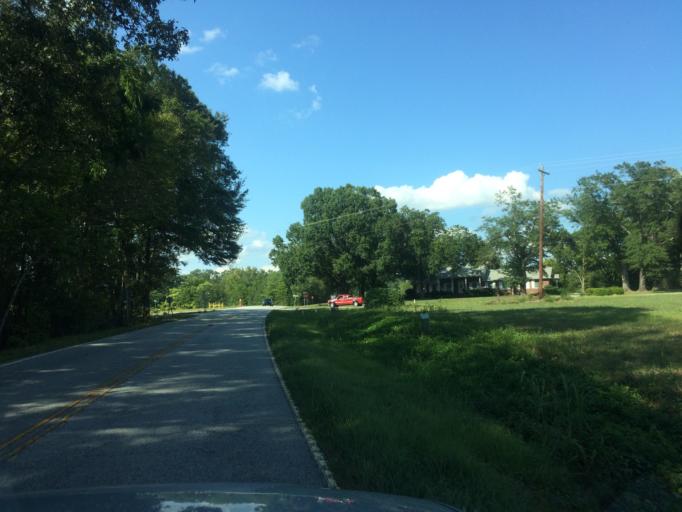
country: US
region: South Carolina
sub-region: Greenwood County
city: Ware Shoals
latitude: 34.4416
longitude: -82.2132
